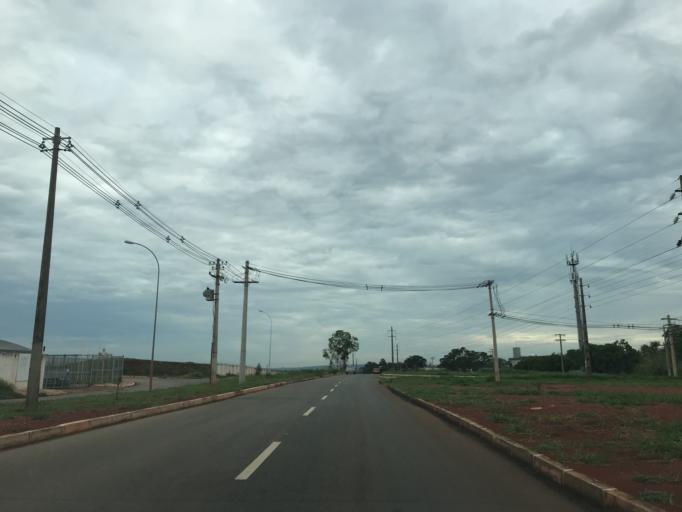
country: BR
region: Federal District
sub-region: Brasilia
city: Brasilia
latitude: -15.7767
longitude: -47.8951
